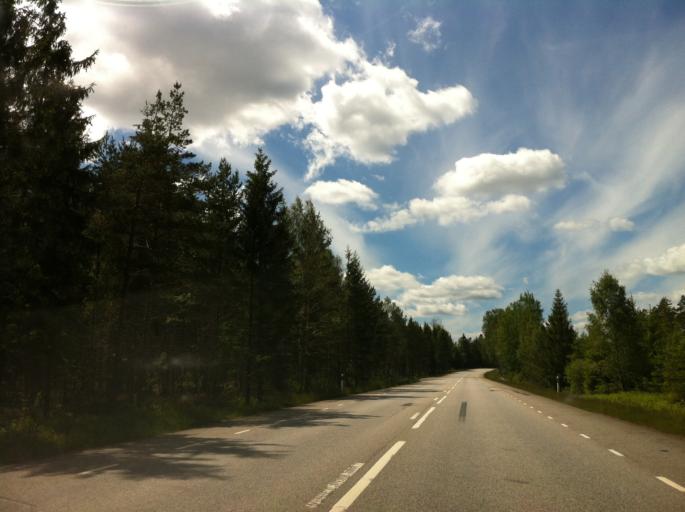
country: SE
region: Vaestra Goetaland
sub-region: Amals Kommun
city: Amal
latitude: 58.9938
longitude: 12.6748
